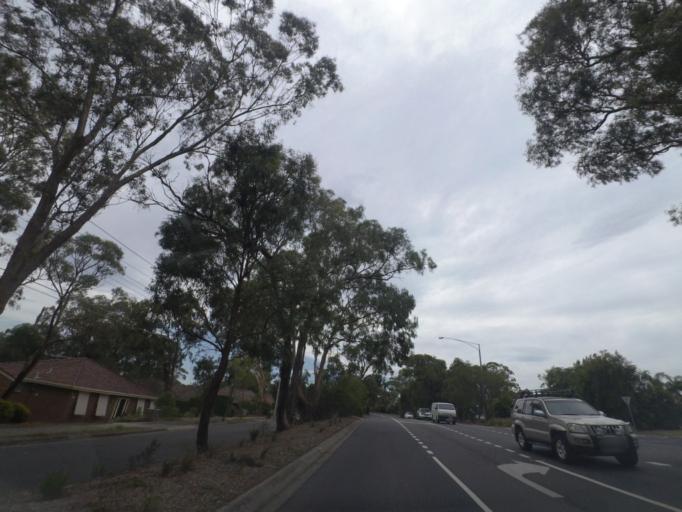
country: AU
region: Victoria
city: Saint Helena
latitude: -37.6960
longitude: 145.1263
